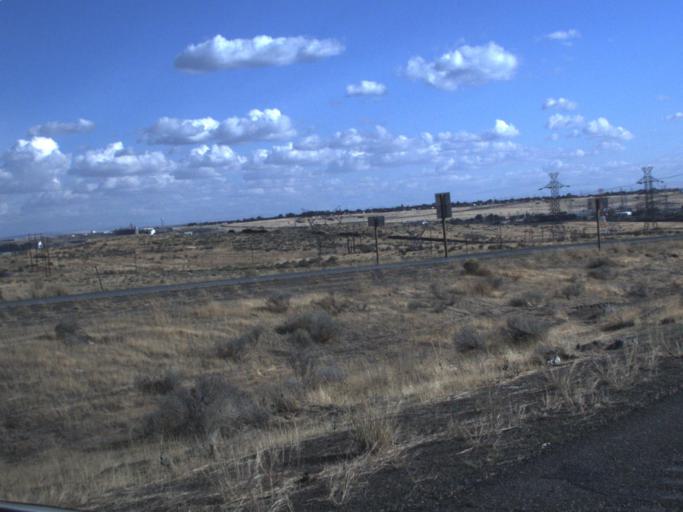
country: US
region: Oregon
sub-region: Umatilla County
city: Umatilla
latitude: 45.9439
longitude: -119.3346
